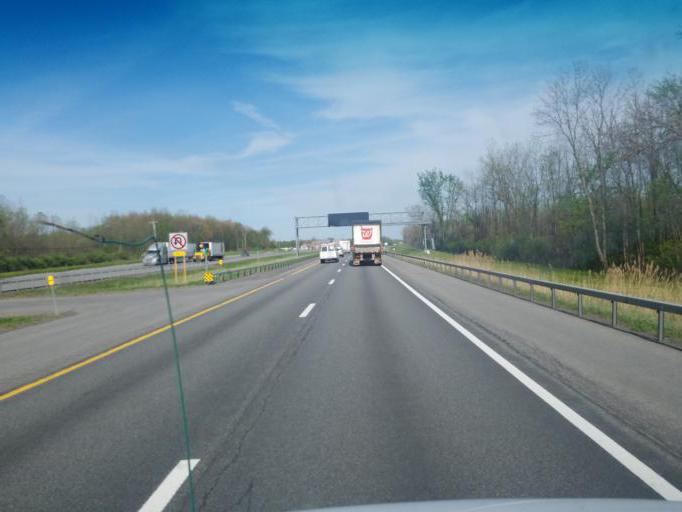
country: US
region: New York
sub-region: Madison County
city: Bolivar
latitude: 43.0956
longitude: -75.8490
